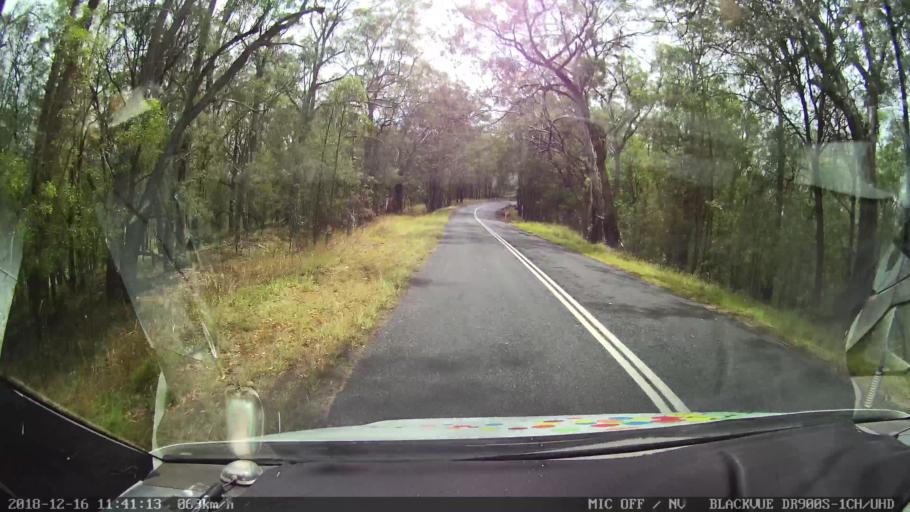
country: AU
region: New South Wales
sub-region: Tenterfield Municipality
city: Carrolls Creek
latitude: -28.9587
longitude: 152.2067
